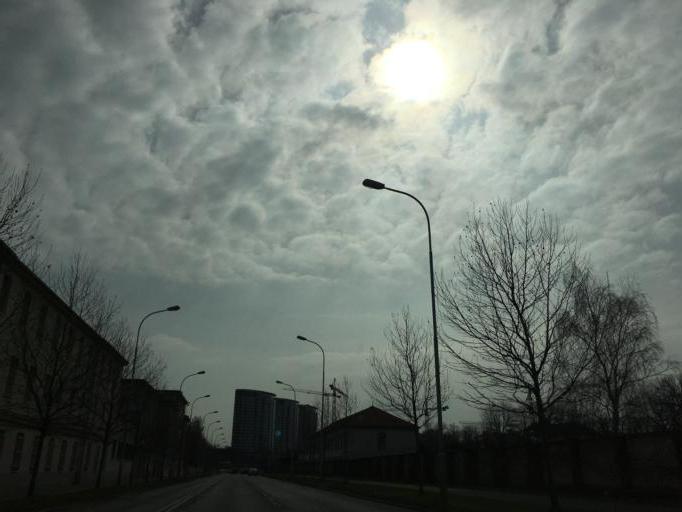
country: SK
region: Bratislavsky
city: Bratislava
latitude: 48.1672
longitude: 17.1324
